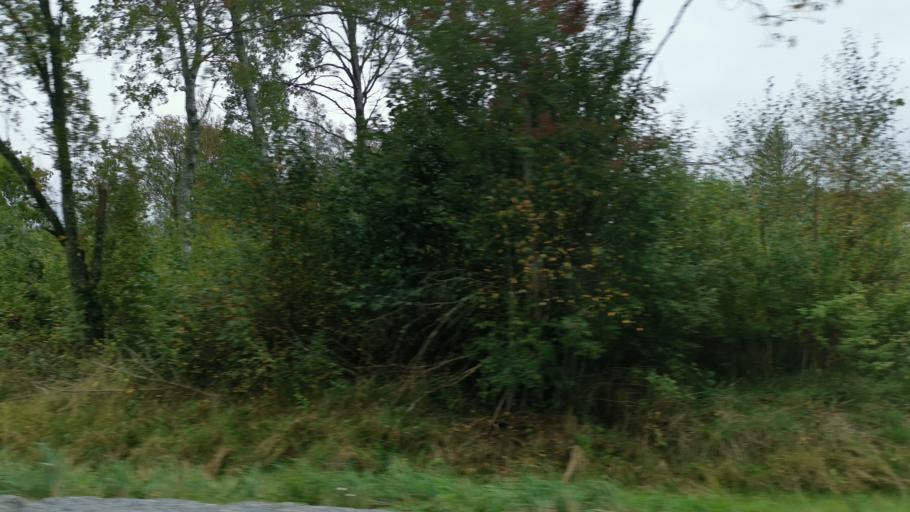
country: SE
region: Vaestra Goetaland
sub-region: Tanums Kommun
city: Tanumshede
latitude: 58.6919
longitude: 11.3357
